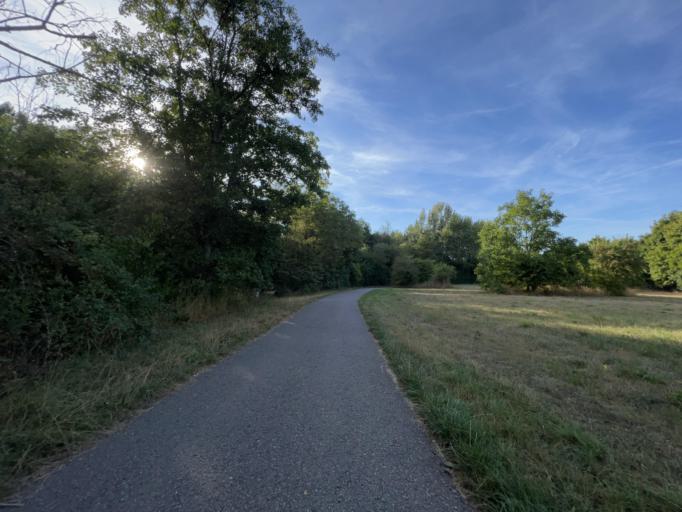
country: DE
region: North Rhine-Westphalia
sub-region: Regierungsbezirk Koln
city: Dueren
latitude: 50.8145
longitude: 6.4575
